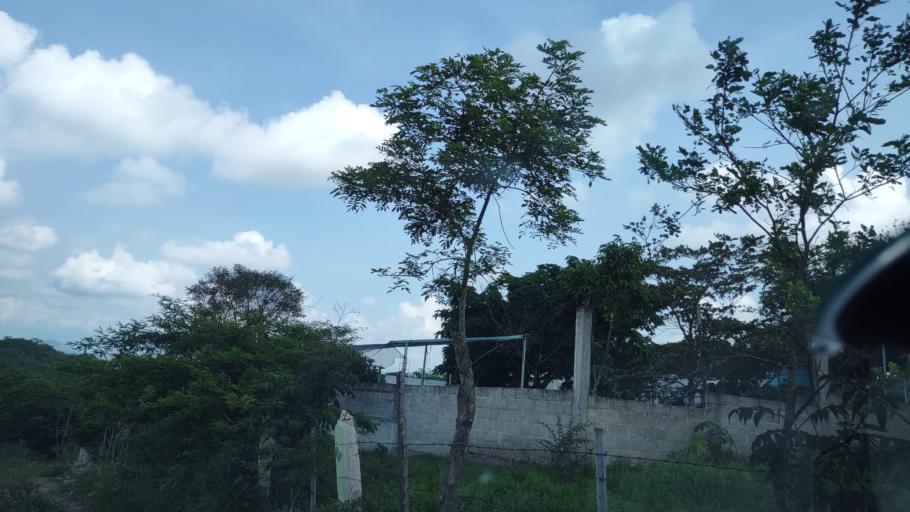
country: MX
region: Veracruz
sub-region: Emiliano Zapata
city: Dos Rios
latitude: 19.4496
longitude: -96.8110
